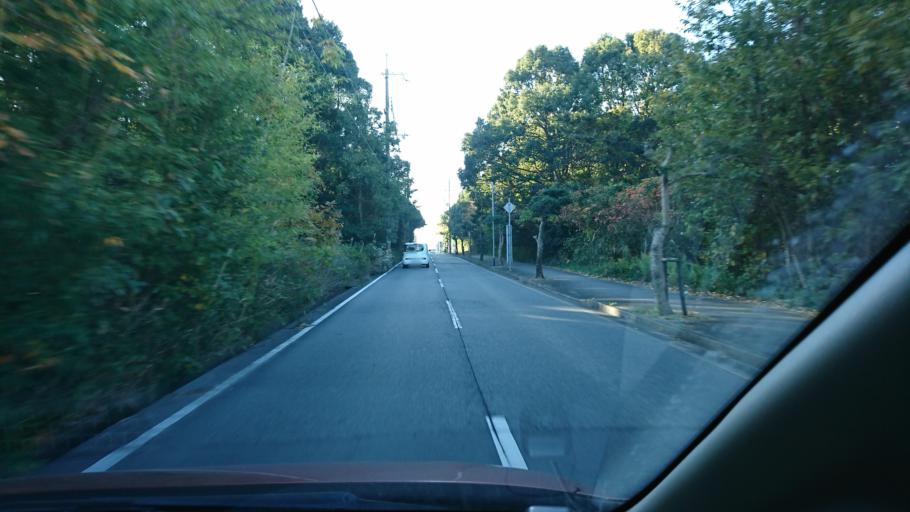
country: JP
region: Hyogo
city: Miki
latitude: 34.7530
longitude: 134.9206
